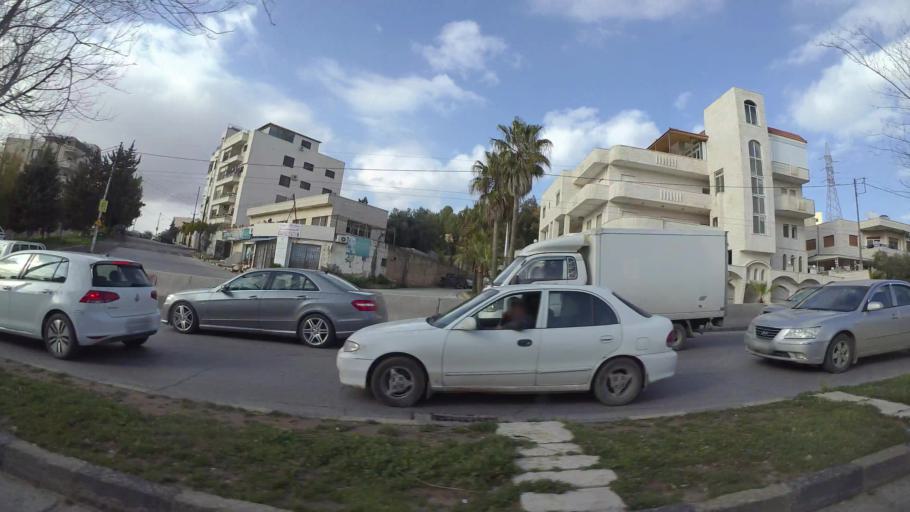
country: JO
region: Amman
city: Umm as Summaq
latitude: 31.8981
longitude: 35.8619
